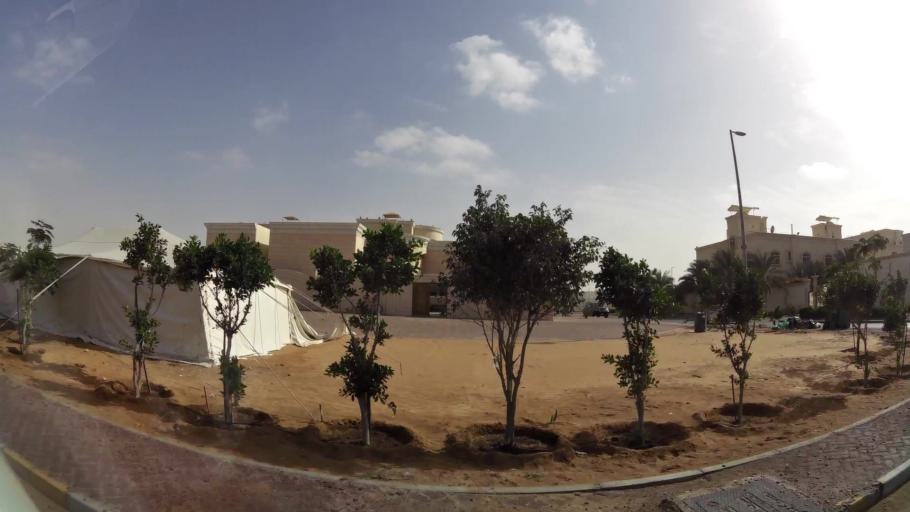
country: AE
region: Abu Dhabi
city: Abu Dhabi
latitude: 24.4302
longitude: 54.5985
